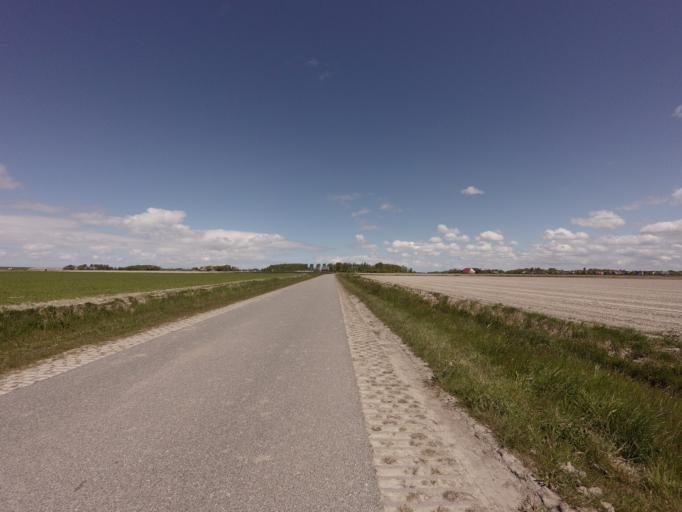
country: NL
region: Friesland
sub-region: Gemeente Harlingen
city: Harlingen
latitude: 53.1380
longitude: 5.4212
